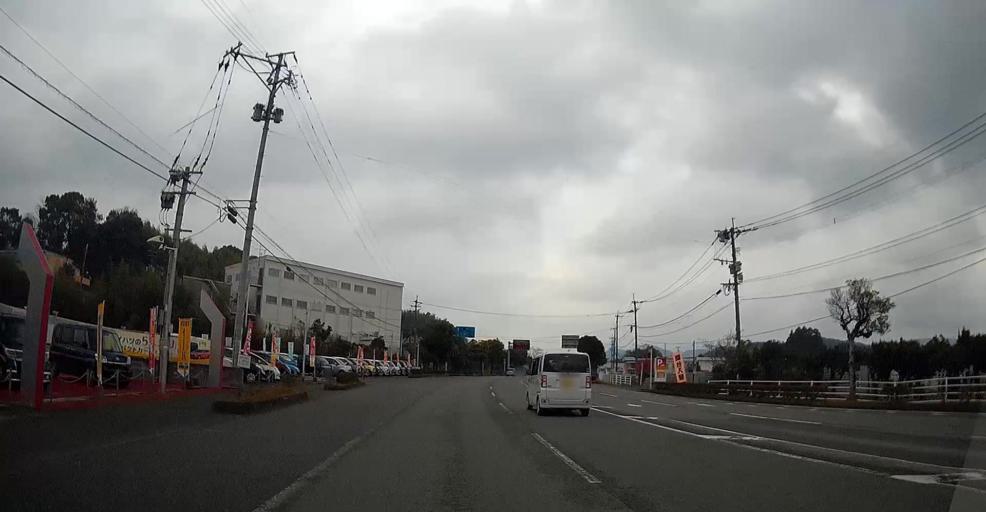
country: JP
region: Kumamoto
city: Matsubase
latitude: 32.6517
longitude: 130.7008
